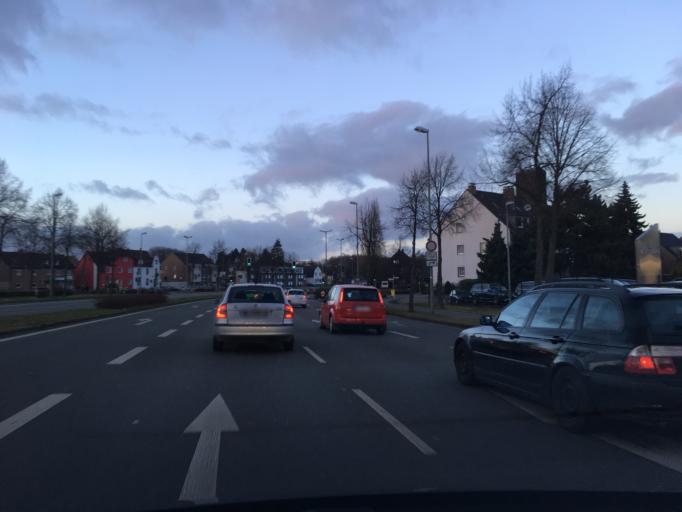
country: DE
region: North Rhine-Westphalia
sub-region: Regierungsbezirk Munster
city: Bottrop
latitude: 51.5438
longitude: 6.9179
